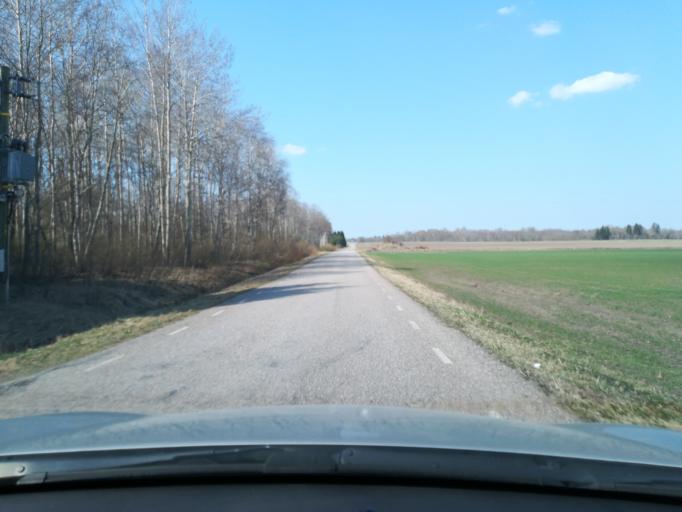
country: EE
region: Harju
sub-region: Saue linn
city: Saue
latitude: 59.3342
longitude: 24.4915
